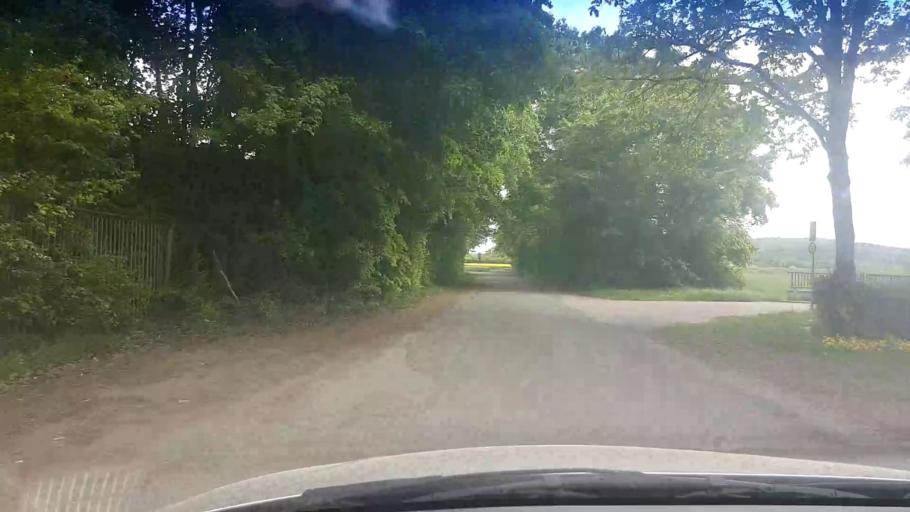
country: DE
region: Bavaria
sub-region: Upper Franconia
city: Bamberg
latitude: 49.8774
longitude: 10.9125
